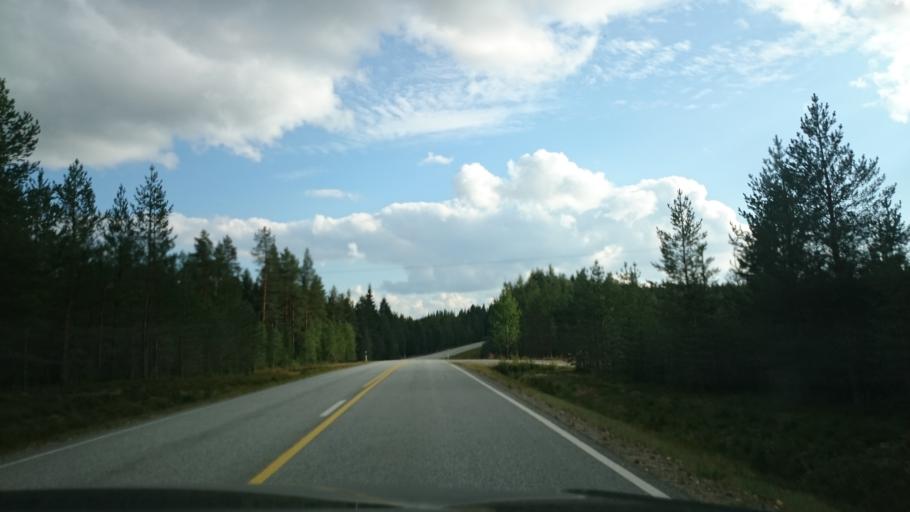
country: FI
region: Kainuu
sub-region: Kehys-Kainuu
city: Kuhmo
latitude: 64.5212
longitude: 29.9462
